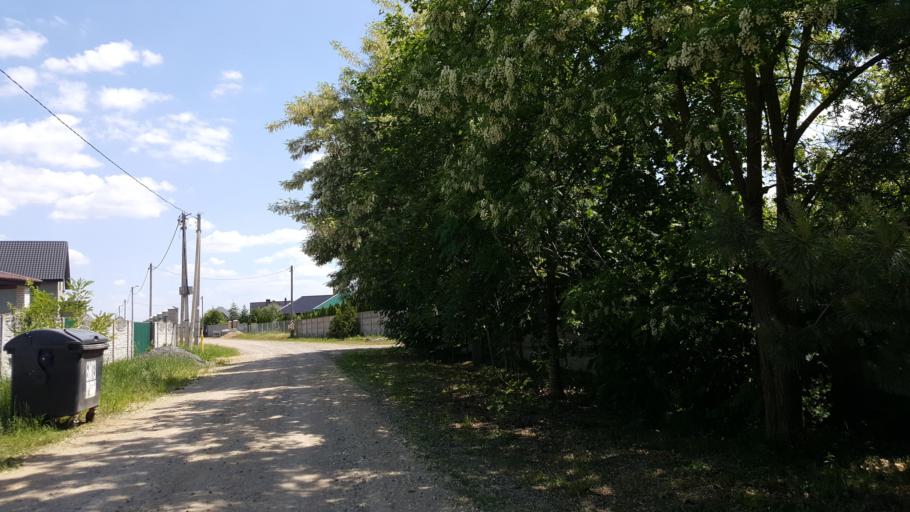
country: BY
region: Brest
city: Zhabinka
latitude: 52.1978
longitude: 24.0606
